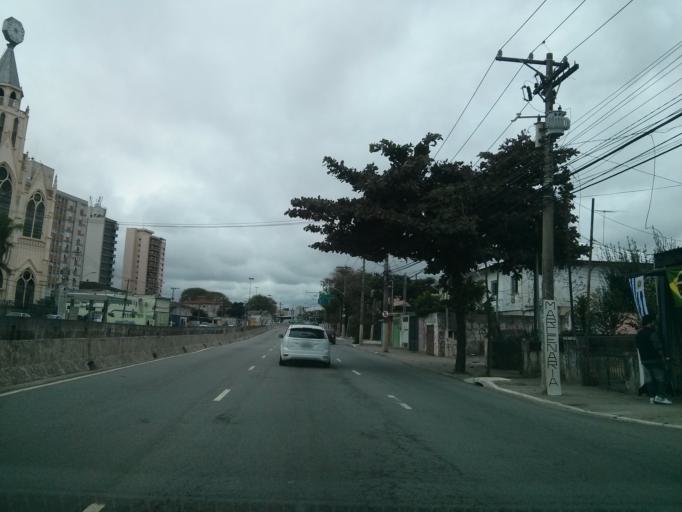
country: BR
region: Sao Paulo
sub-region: Sao Paulo
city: Sao Paulo
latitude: -23.5804
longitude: -46.6131
